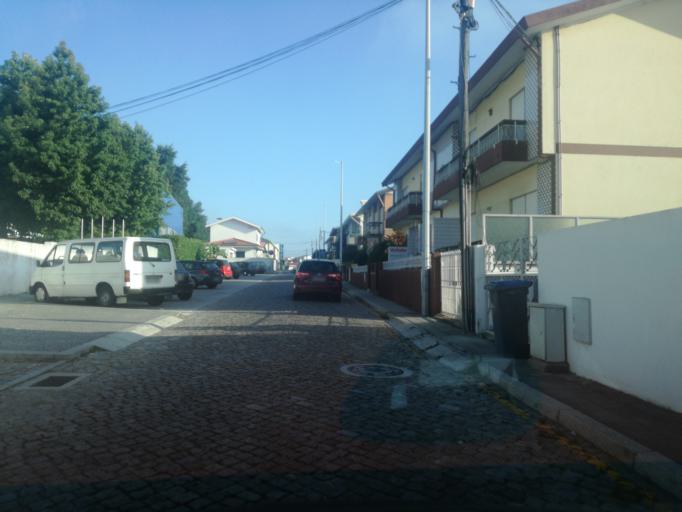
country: PT
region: Porto
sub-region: Maia
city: Gemunde
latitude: 41.2480
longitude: -8.6584
